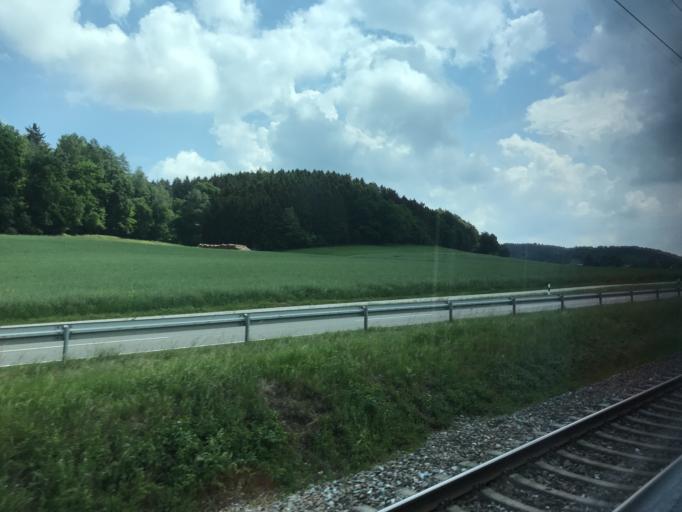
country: DE
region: Bavaria
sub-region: Swabia
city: Durrlauingen
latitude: 48.4669
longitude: 10.3964
